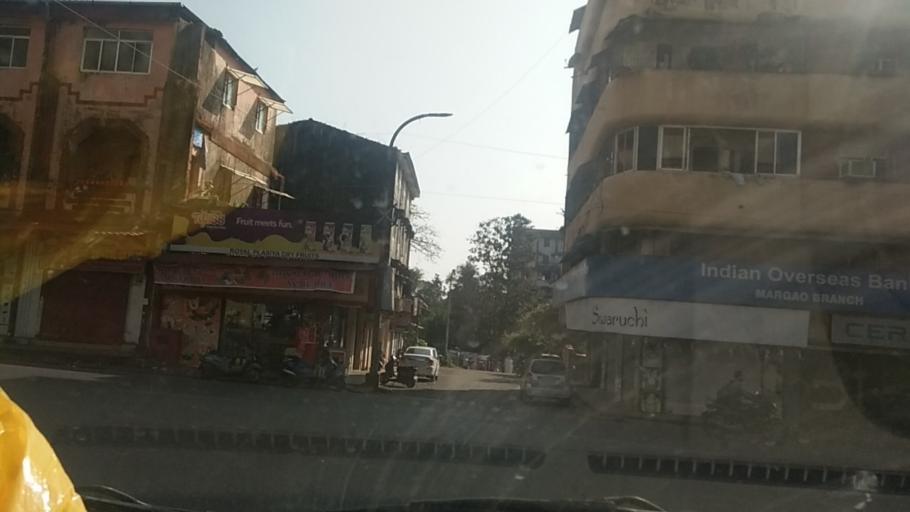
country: IN
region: Goa
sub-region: South Goa
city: Madgaon
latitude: 15.2718
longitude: 73.9647
